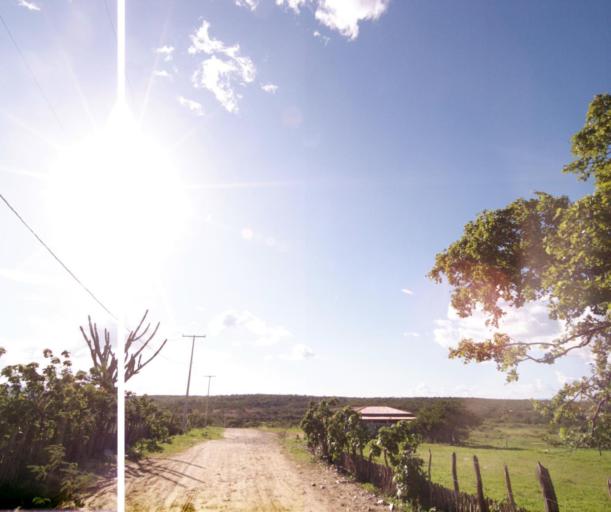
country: BR
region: Bahia
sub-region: Tanhacu
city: Tanhacu
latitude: -14.1828
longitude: -41.0129
